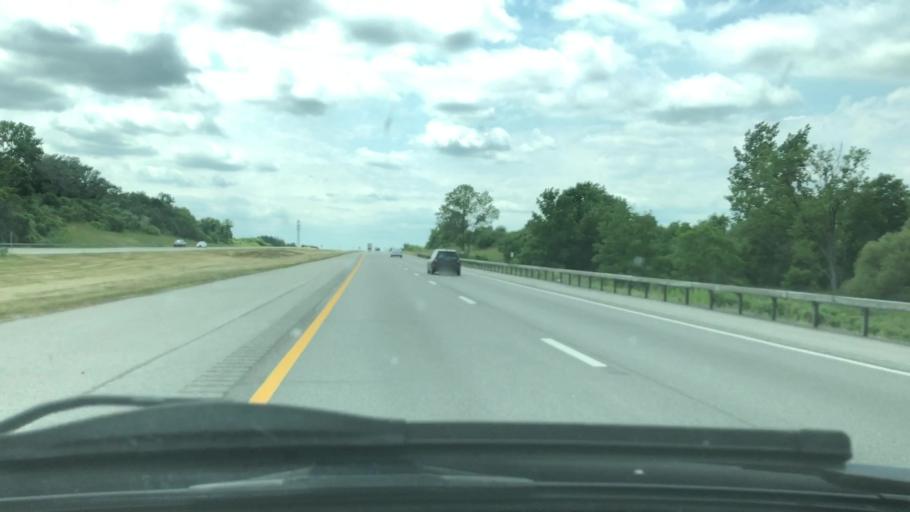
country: US
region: New York
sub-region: Genesee County
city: Le Roy
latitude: 43.0182
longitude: -78.0818
